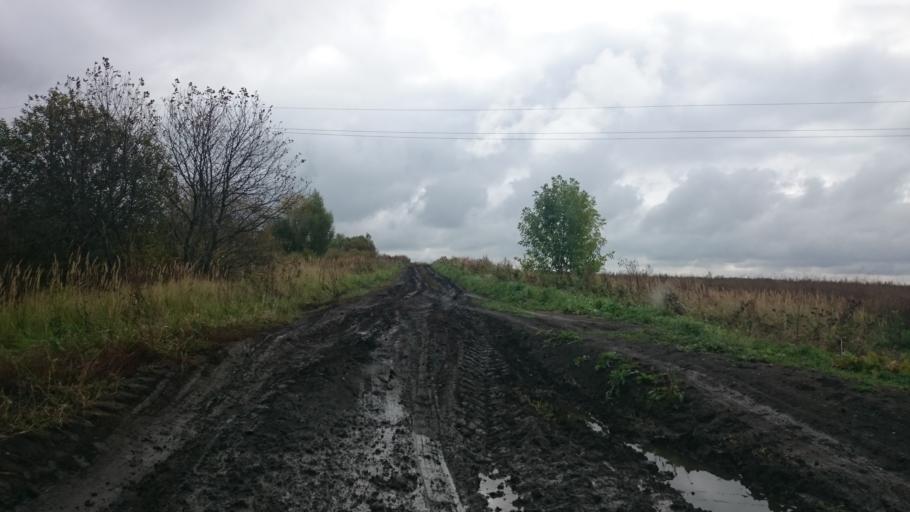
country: RU
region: Mordoviya
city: Kadoshkino
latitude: 54.0164
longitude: 44.4612
